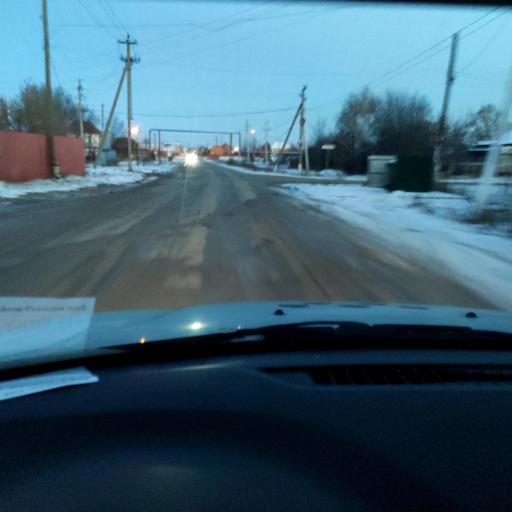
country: RU
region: Samara
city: Tol'yatti
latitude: 53.5691
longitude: 49.3941
